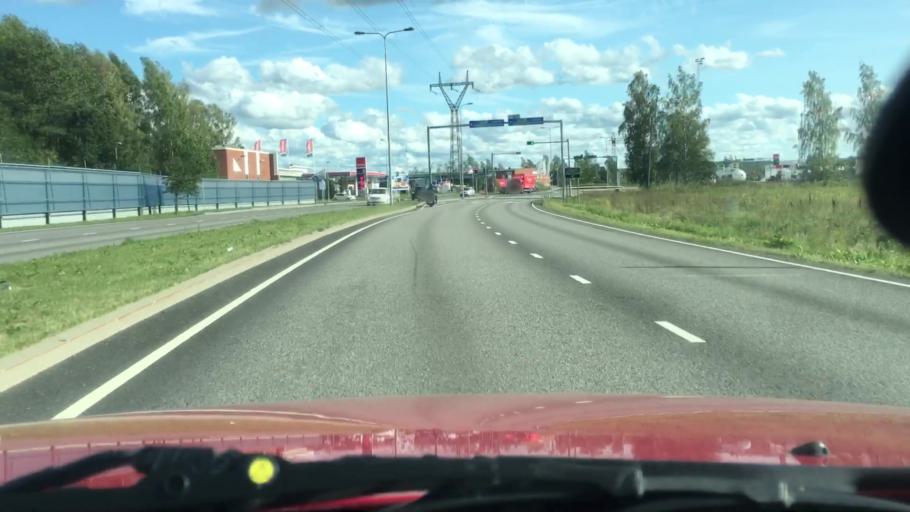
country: FI
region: Varsinais-Suomi
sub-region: Turku
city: Raisio
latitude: 60.4510
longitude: 22.2000
